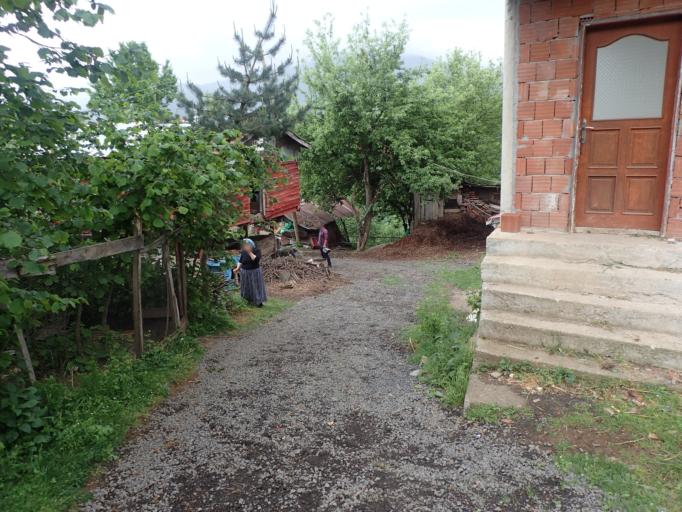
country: TR
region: Ordu
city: Akkus
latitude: 40.9048
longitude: 36.8729
